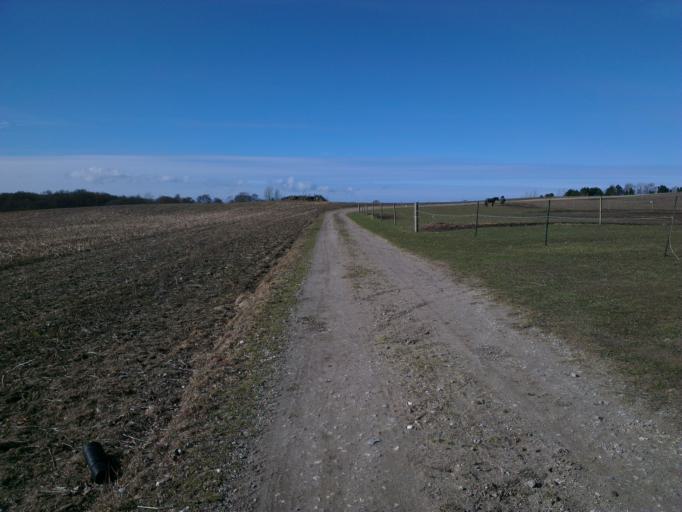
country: DK
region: Capital Region
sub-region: Frederikssund Kommune
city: Jaegerspris
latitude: 55.8378
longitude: 11.9799
